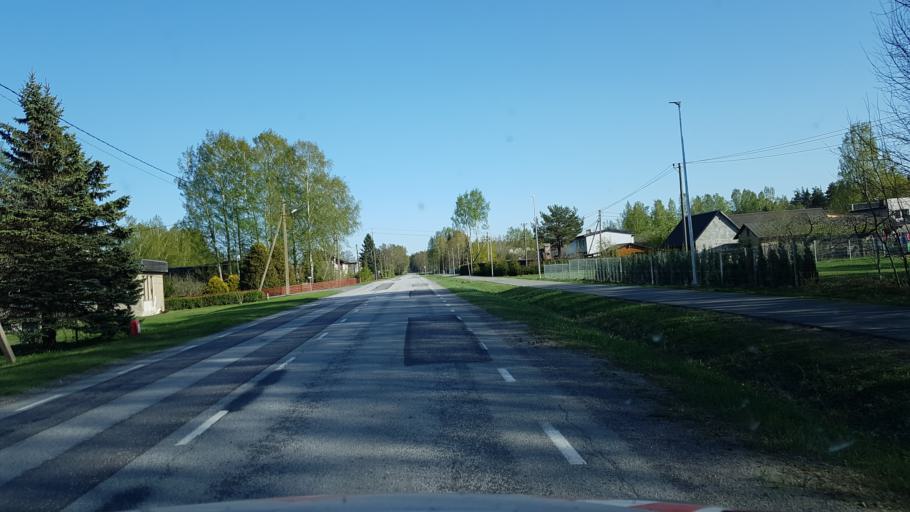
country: EE
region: Paernumaa
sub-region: Paikuse vald
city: Paikuse
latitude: 58.3713
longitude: 24.6312
